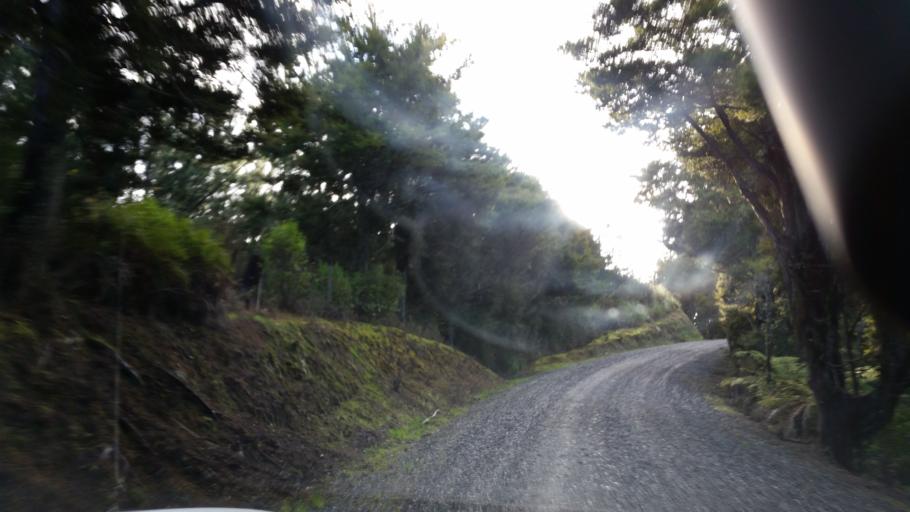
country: NZ
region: Northland
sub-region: Whangarei
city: Maungatapere
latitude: -35.7876
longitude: 174.0796
